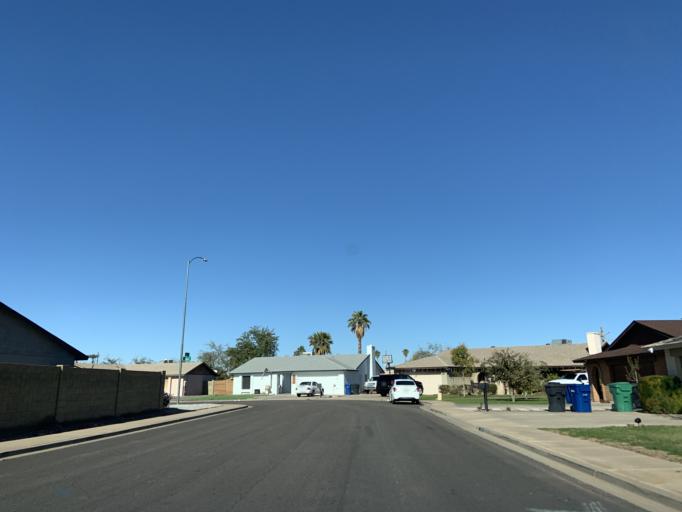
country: US
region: Arizona
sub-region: Maricopa County
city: San Carlos
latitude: 33.3618
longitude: -111.8566
